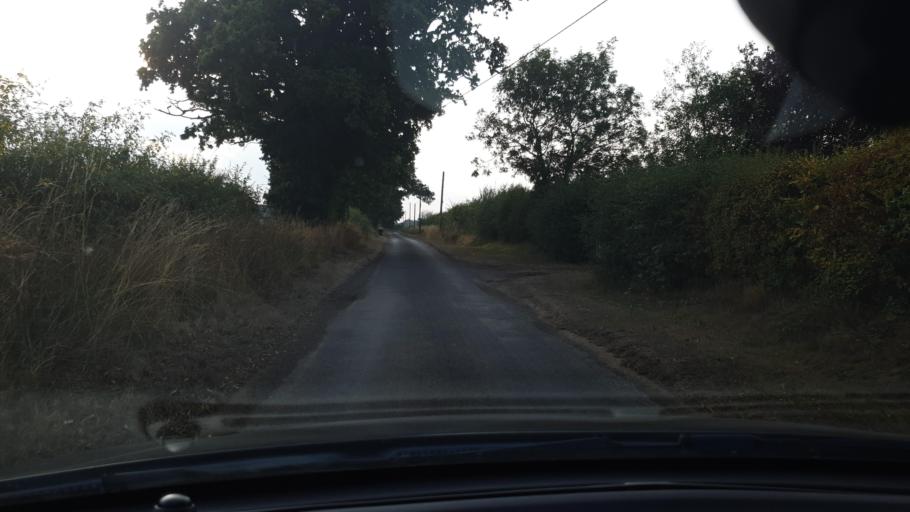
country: GB
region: England
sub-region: Essex
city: Alresford
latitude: 51.9034
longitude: 1.0242
